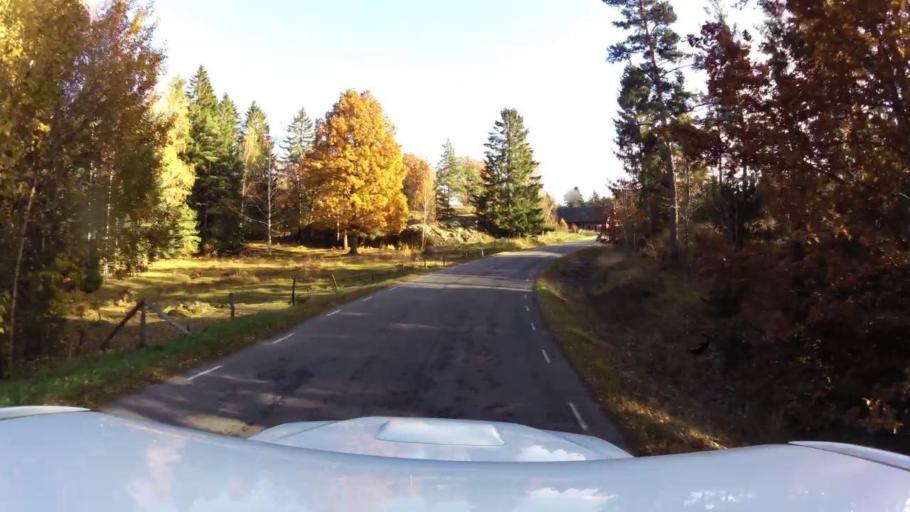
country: SE
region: OEstergoetland
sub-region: Linkopings Kommun
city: Vikingstad
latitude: 58.2688
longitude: 15.4455
